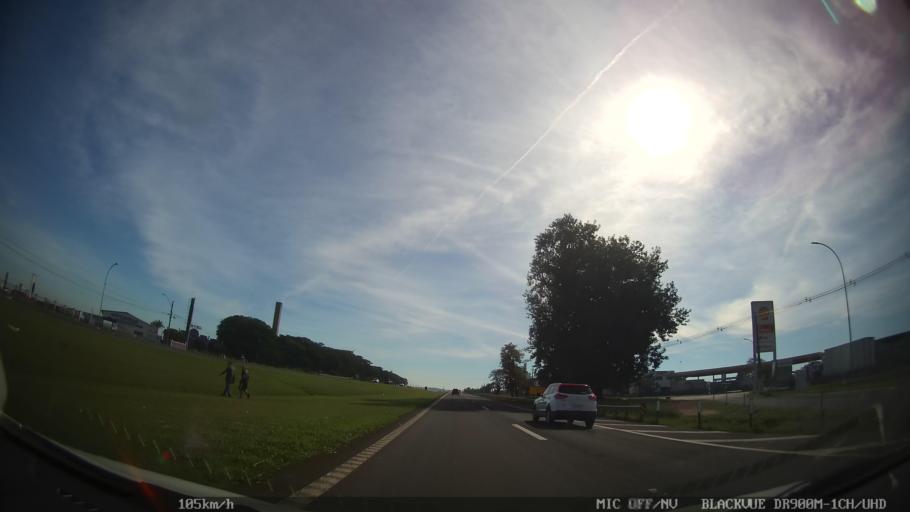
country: BR
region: Sao Paulo
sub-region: Araras
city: Araras
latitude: -22.4110
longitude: -47.3897
